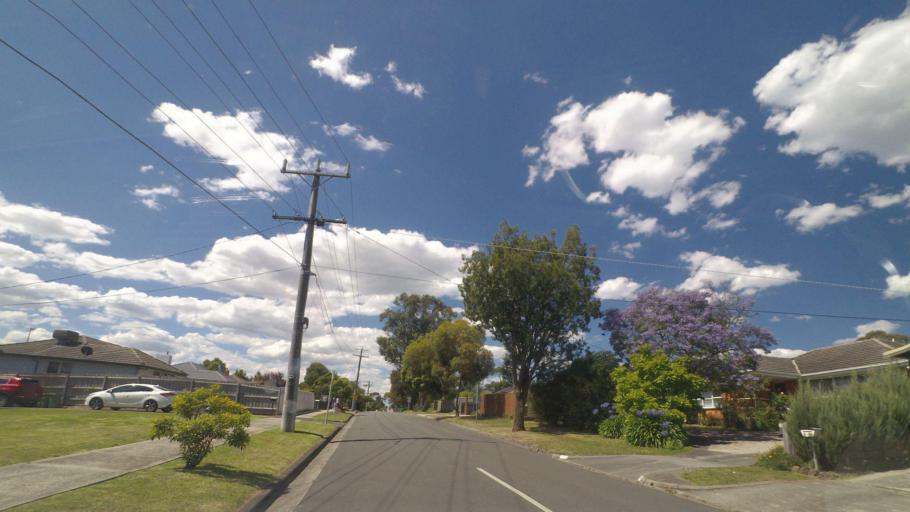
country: AU
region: Victoria
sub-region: Yarra Ranges
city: Kilsyth
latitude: -37.8086
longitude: 145.3245
